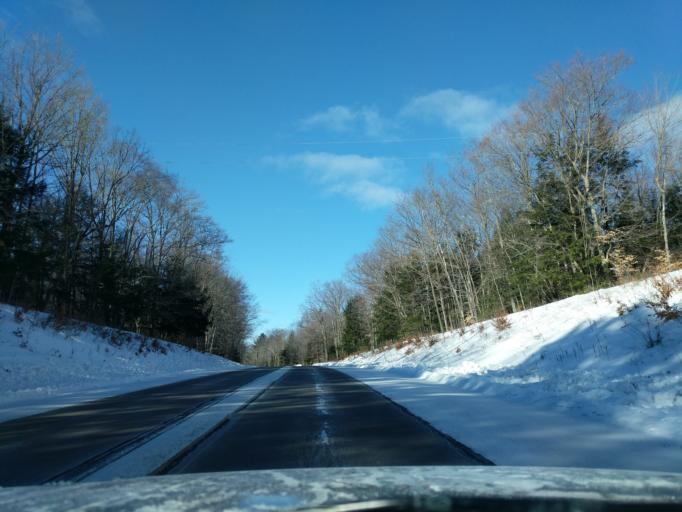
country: US
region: Wisconsin
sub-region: Menominee County
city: Keshena
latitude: 45.1468
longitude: -88.6835
